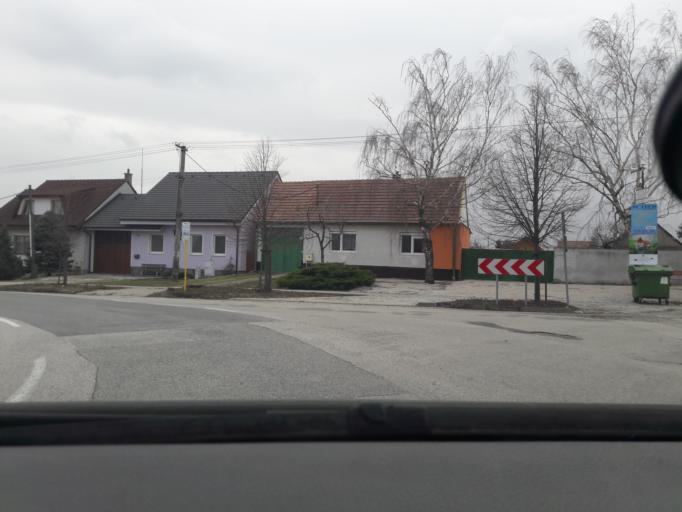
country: SK
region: Trnavsky
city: Smolenice
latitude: 48.4157
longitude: 17.3790
